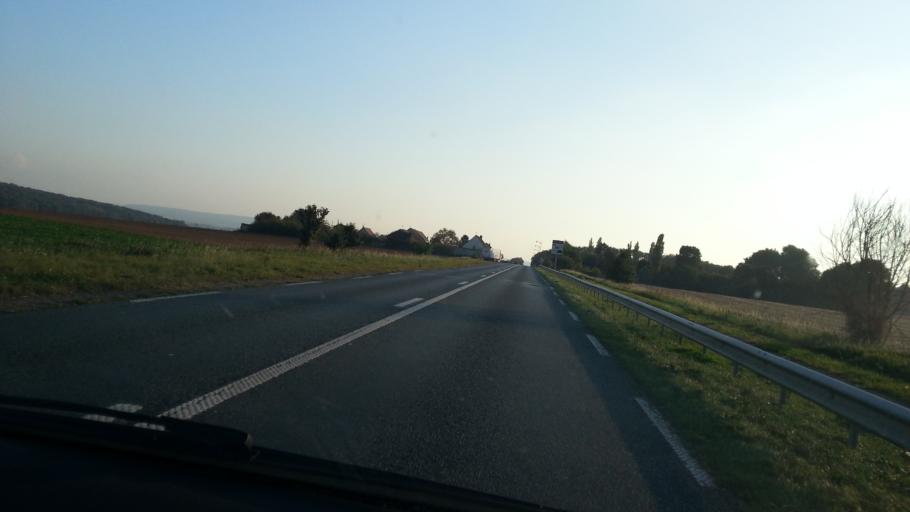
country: FR
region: Picardie
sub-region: Departement de l'Oise
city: Grandfresnoy
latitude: 49.3885
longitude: 2.6215
